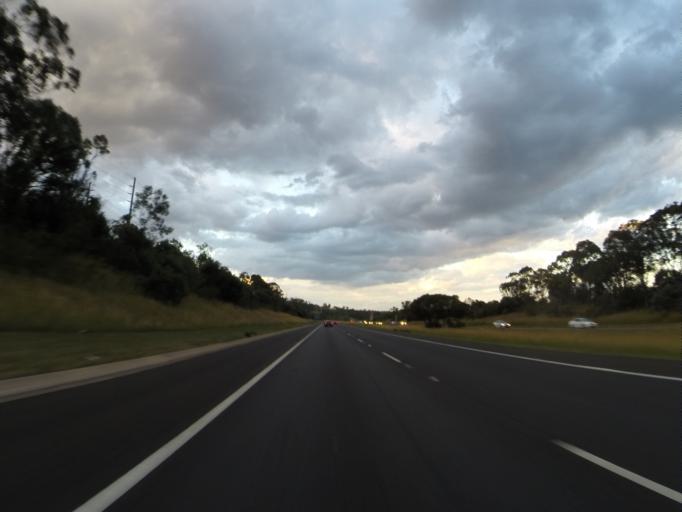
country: AU
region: New South Wales
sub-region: Campbelltown Municipality
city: Glen Alpine
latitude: -34.0703
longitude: 150.7781
